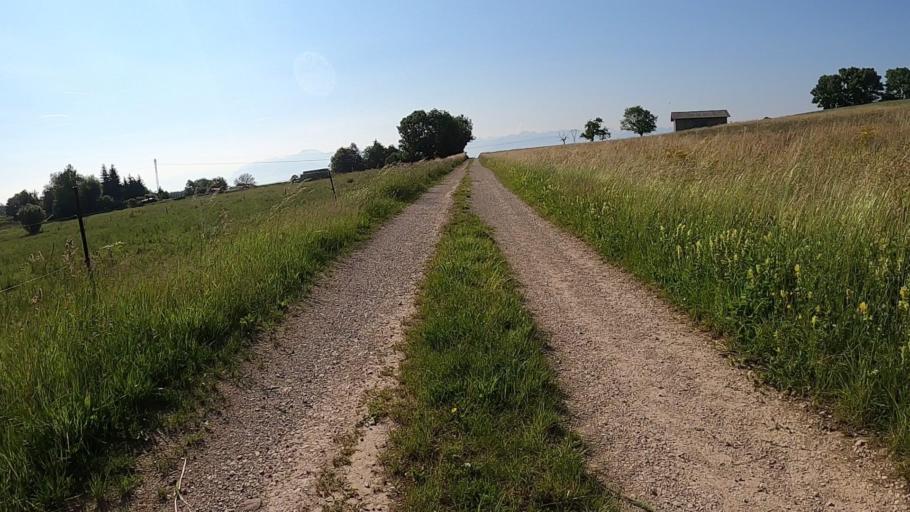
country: CH
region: Vaud
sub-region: Nyon District
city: Rolle
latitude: 46.4854
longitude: 6.3330
